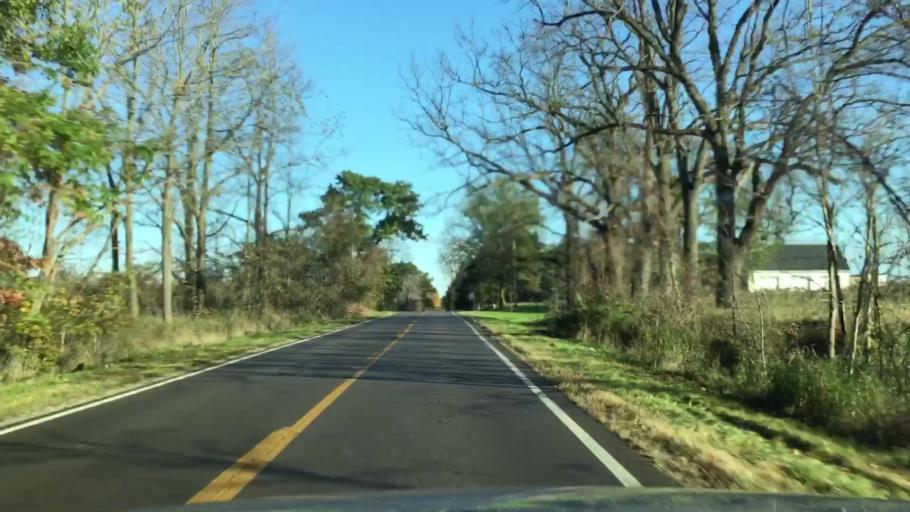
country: US
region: Michigan
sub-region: Genesee County
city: Argentine
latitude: 42.7690
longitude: -83.9417
